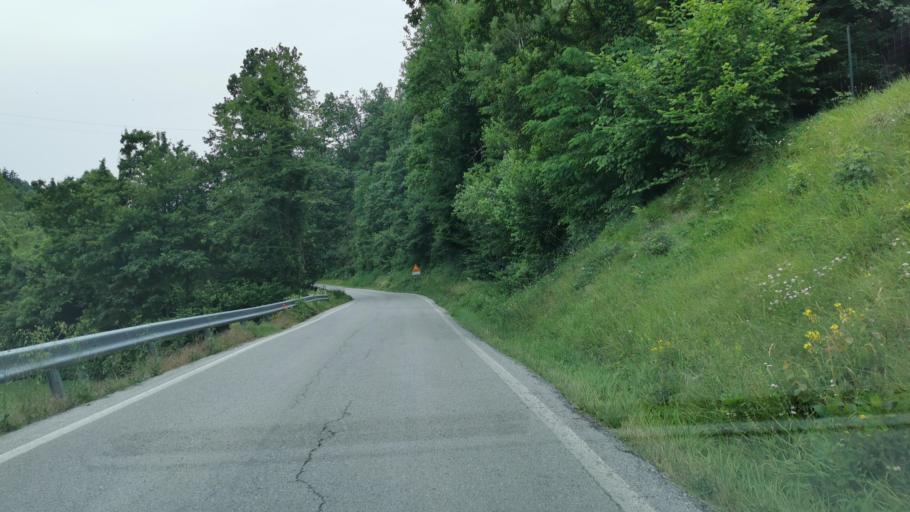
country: IT
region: Piedmont
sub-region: Provincia di Cuneo
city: Torresina
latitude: 44.4098
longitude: 8.0479
